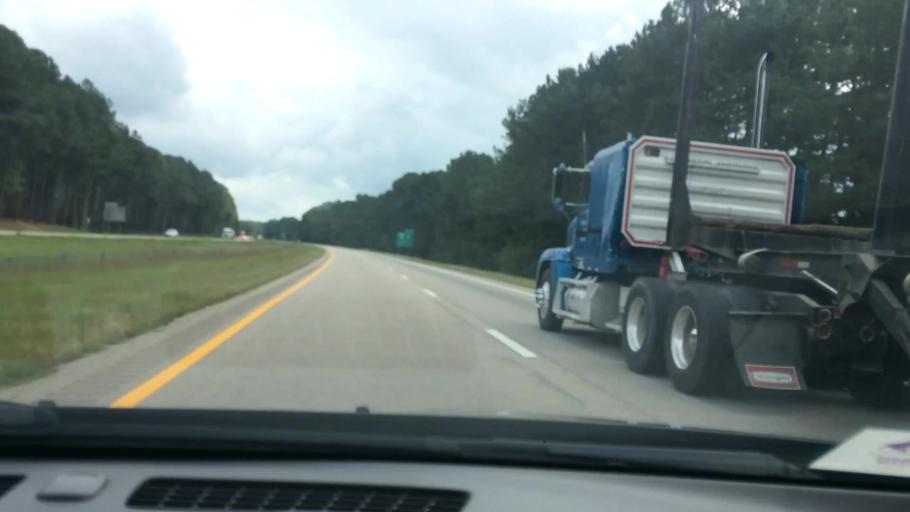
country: US
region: North Carolina
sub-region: Wake County
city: Zebulon
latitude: 35.8244
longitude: -78.2819
